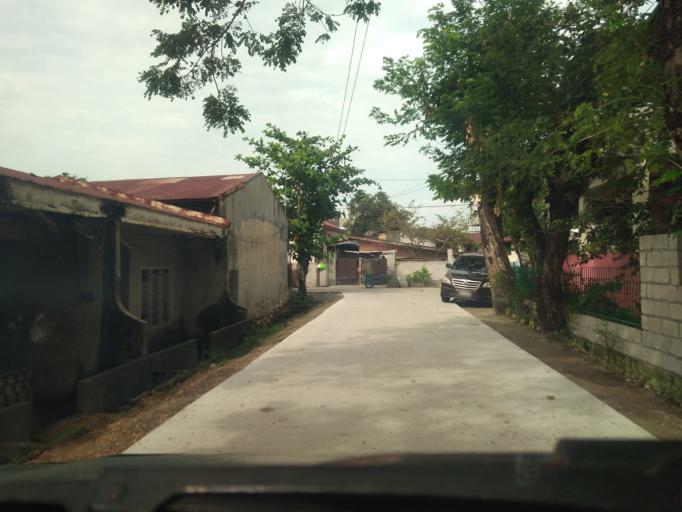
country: PH
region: Central Luzon
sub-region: Province of Pampanga
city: Pau
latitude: 15.0108
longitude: 120.7130
